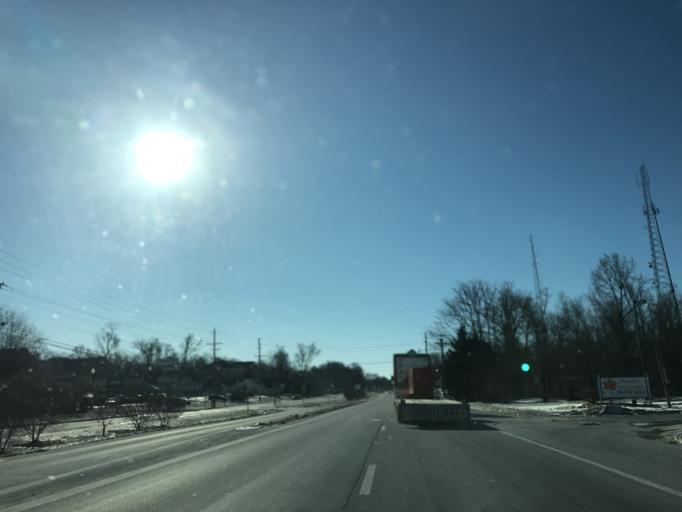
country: US
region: Maryland
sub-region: Charles County
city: La Plata
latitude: 38.5277
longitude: -76.9827
